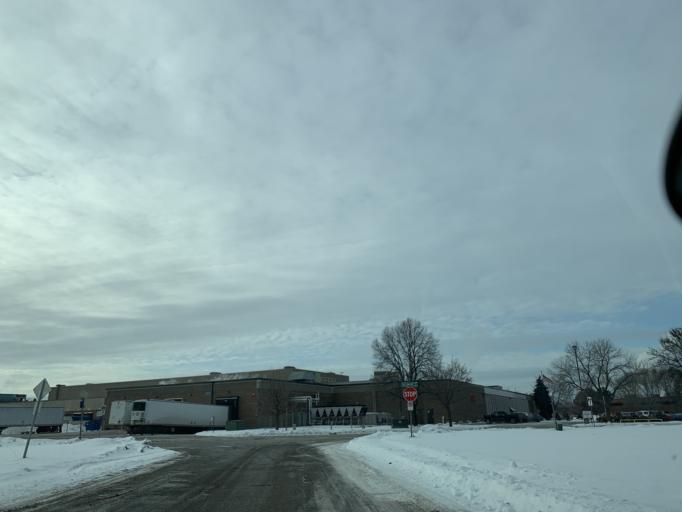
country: US
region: Minnesota
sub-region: Ramsey County
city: Saint Paul
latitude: 44.9439
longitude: -93.0735
